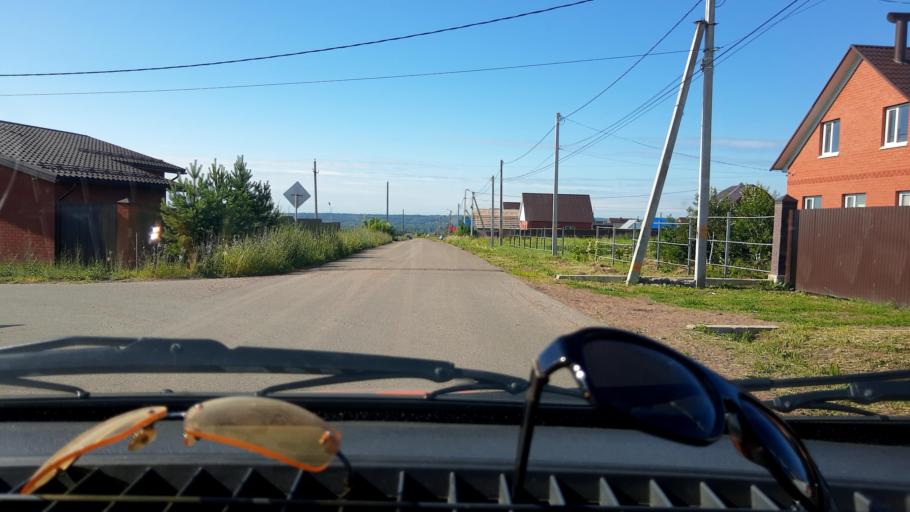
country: RU
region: Bashkortostan
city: Avdon
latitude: 54.6539
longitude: 55.7375
